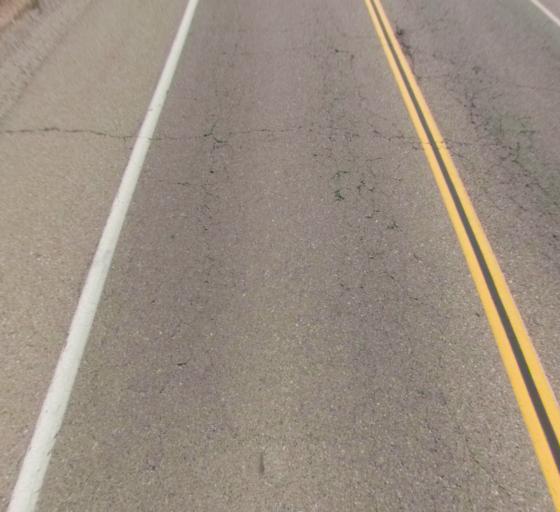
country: US
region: California
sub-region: Fresno County
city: Biola
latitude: 36.8501
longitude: -120.0715
